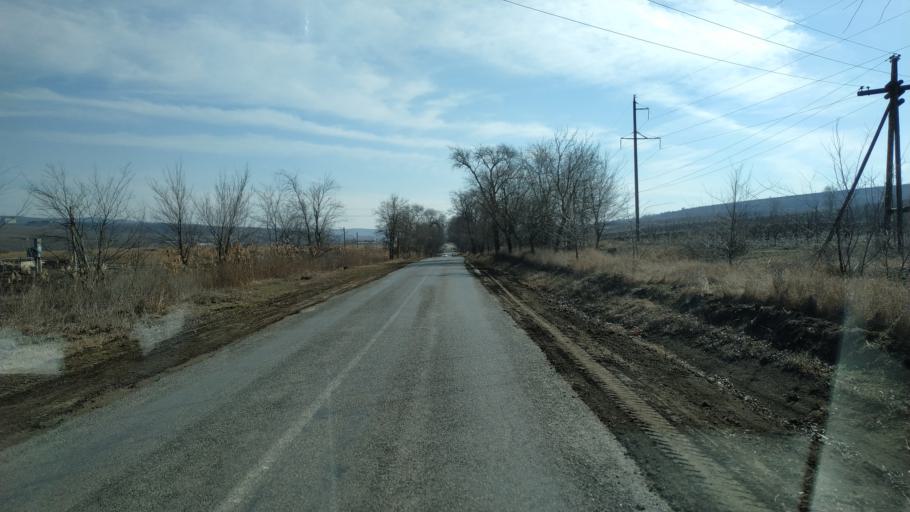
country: MD
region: Nisporeni
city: Nisporeni
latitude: 47.0929
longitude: 28.1353
